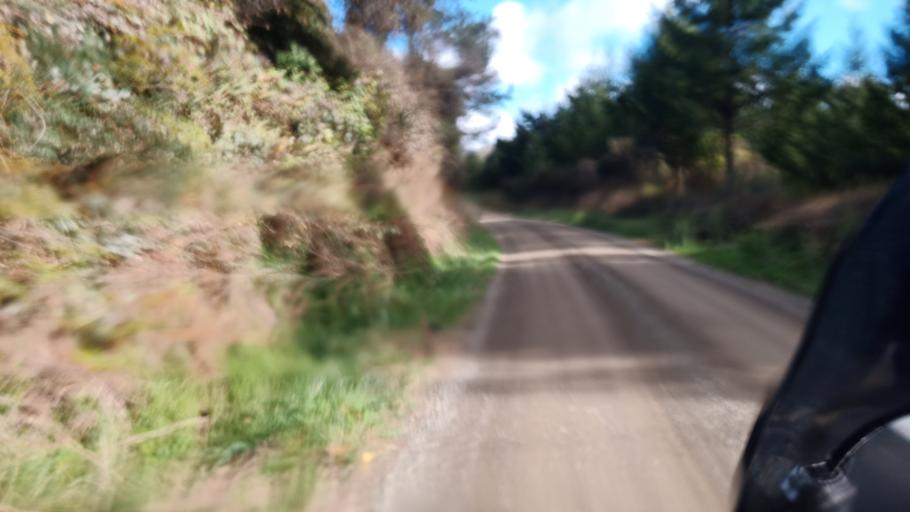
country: NZ
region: Bay of Plenty
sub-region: Opotiki District
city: Opotiki
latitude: -38.4581
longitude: 177.4106
